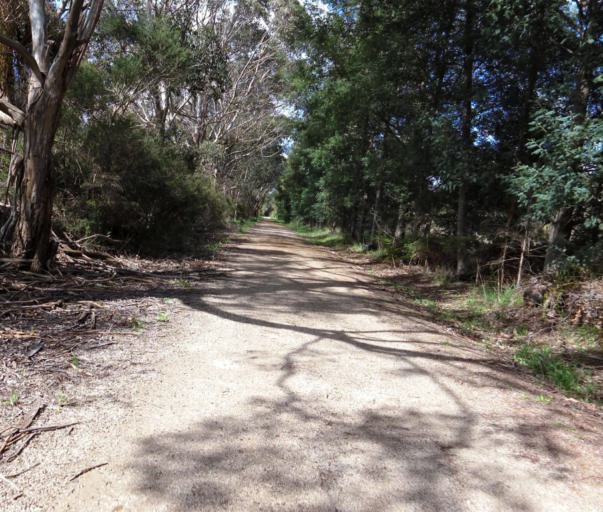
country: AU
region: Victoria
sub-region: Bass Coast
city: North Wonthaggi
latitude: -38.5867
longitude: 146.0375
